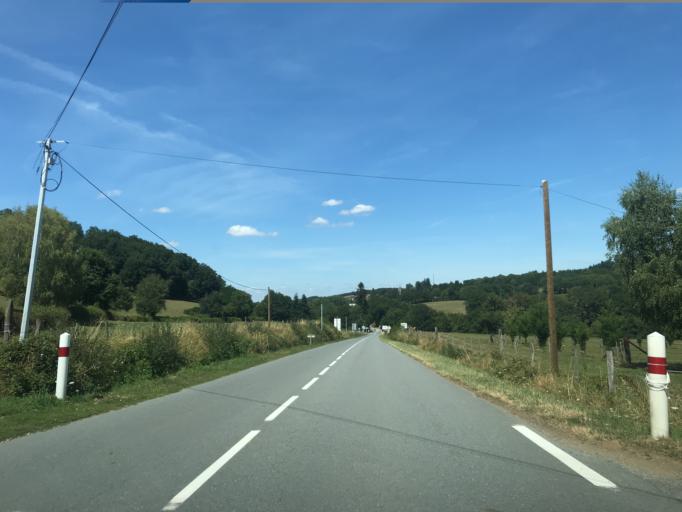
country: FR
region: Limousin
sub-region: Departement de la Creuse
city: Felletin
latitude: 45.8672
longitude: 2.1704
